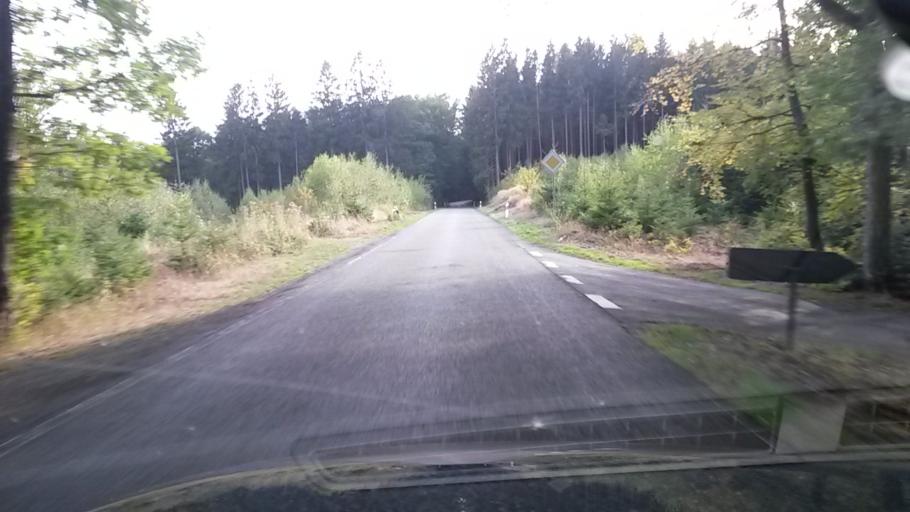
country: DE
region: North Rhine-Westphalia
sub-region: Regierungsbezirk Arnsberg
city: Herscheid
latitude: 51.1954
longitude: 7.7526
